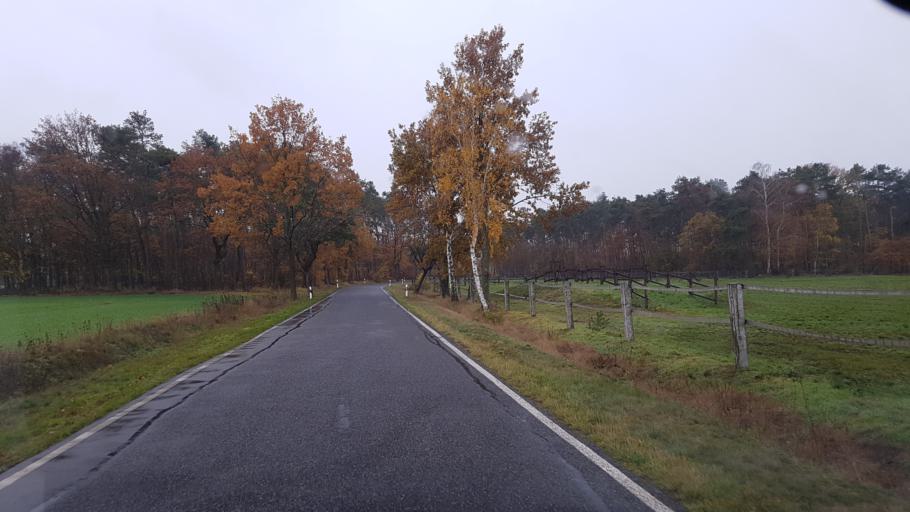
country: DE
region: Brandenburg
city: Herzberg
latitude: 51.6646
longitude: 13.2269
